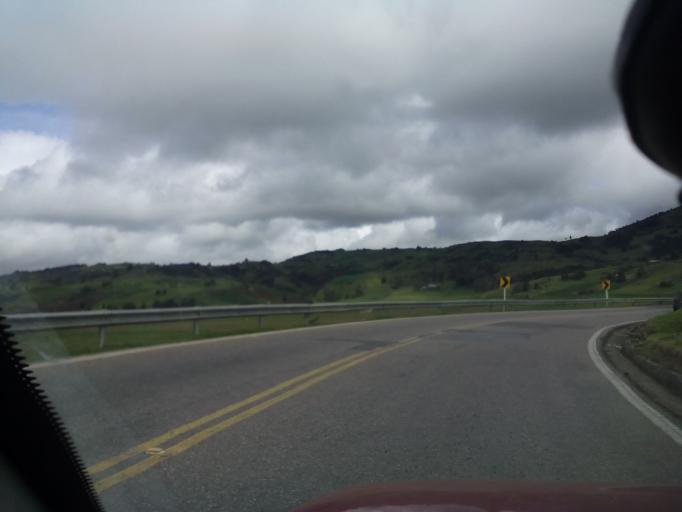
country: CO
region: Boyaca
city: Combita
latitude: 5.6579
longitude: -73.3588
